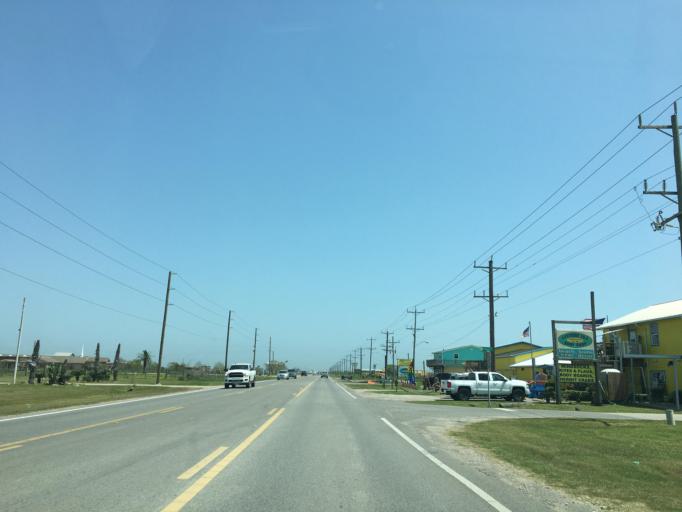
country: US
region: Texas
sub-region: Galveston County
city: Bolivar Peninsula
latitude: 29.4493
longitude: -94.6542
